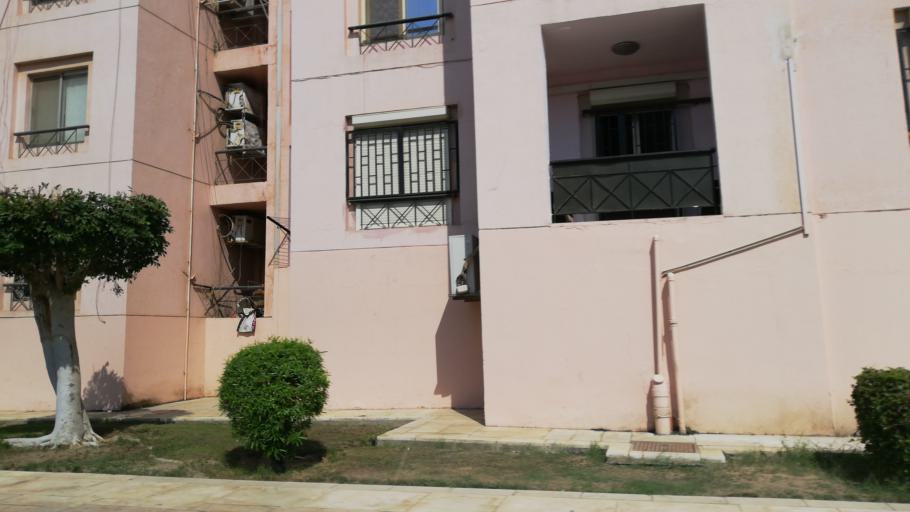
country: EG
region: Muhafazat al Qalyubiyah
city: Al Khankah
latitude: 30.0597
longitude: 31.4877
